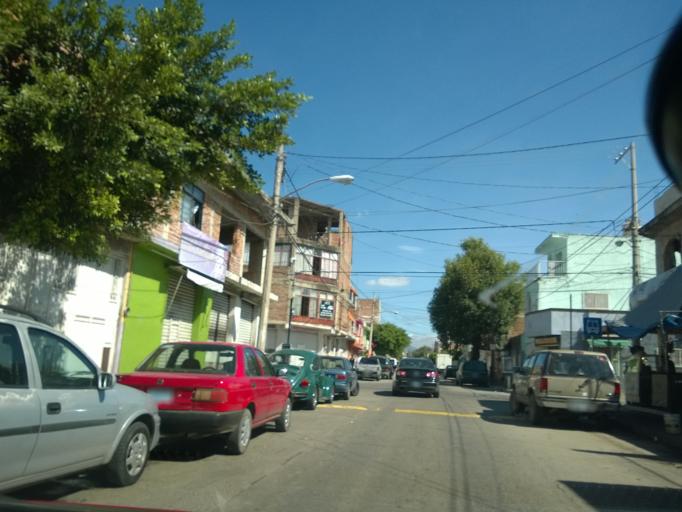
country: MX
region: Guanajuato
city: Leon
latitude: 21.1069
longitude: -101.6804
